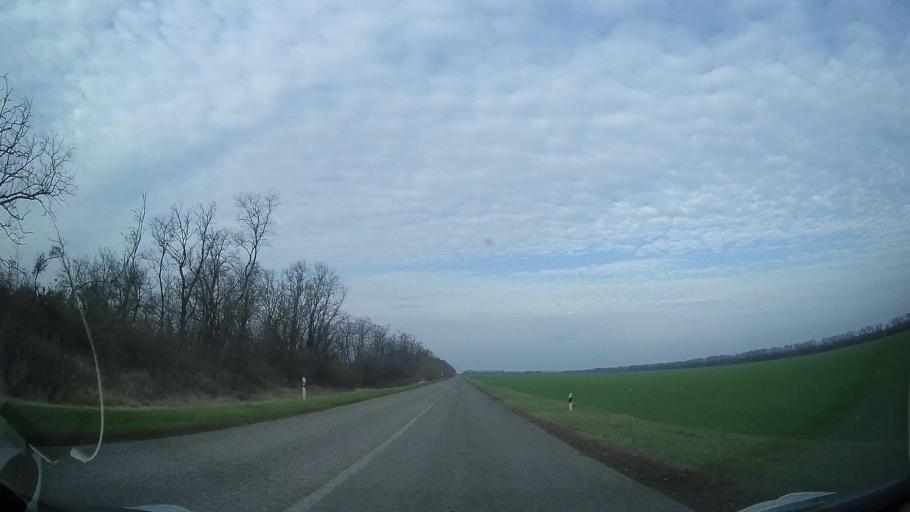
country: RU
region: Rostov
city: Zernograd
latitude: 46.9676
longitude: 40.3916
